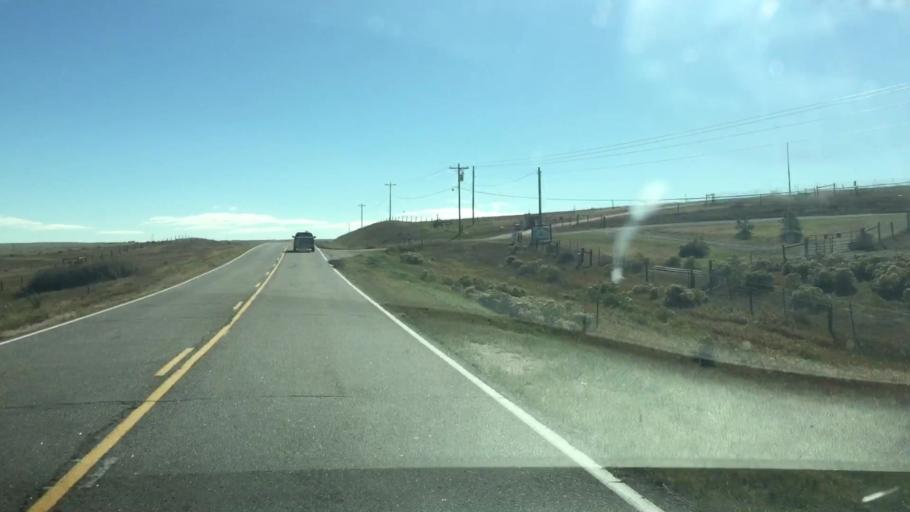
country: US
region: Colorado
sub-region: Elbert County
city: Kiowa
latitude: 39.3515
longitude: -104.4929
